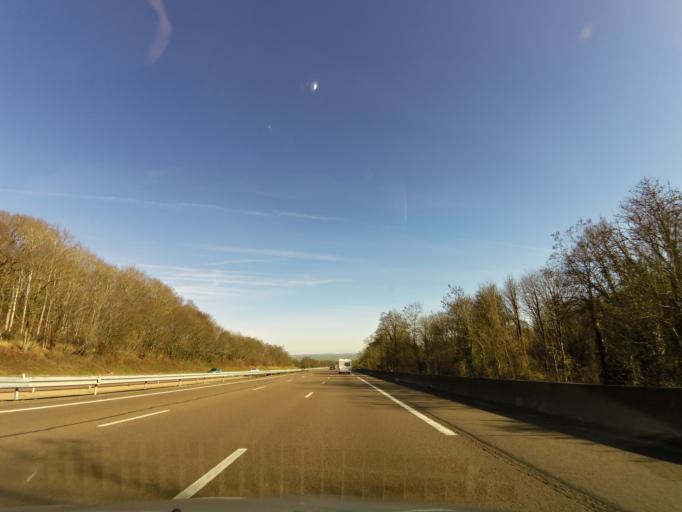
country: FR
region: Bourgogne
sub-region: Departement de l'Yonne
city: Aillant-sur-Tholon
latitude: 47.9102
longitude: 3.3120
